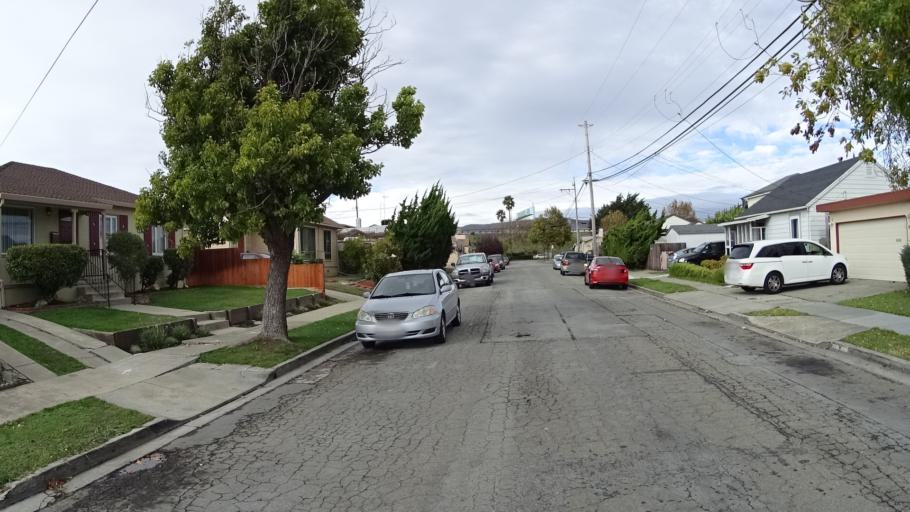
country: US
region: California
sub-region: San Mateo County
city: San Bruno
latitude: 37.6321
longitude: -122.4077
